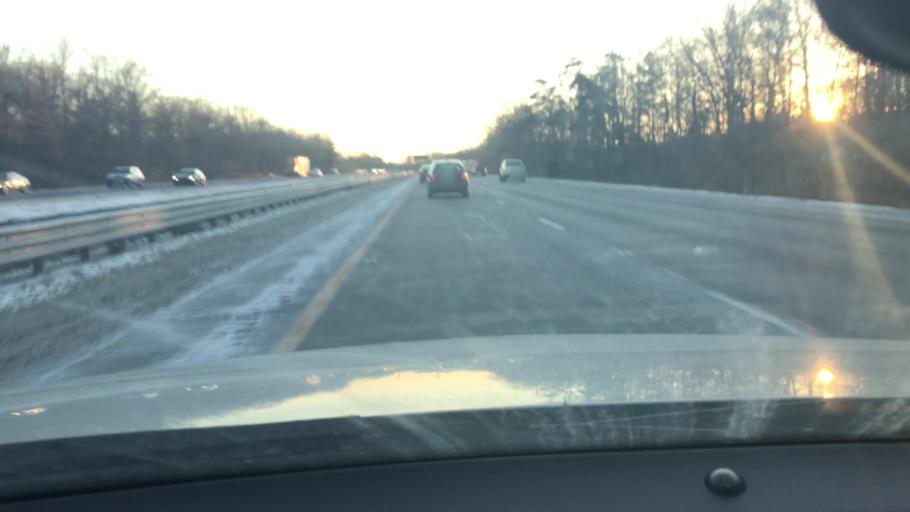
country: US
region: New Jersey
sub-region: Mercer County
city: Mercerville
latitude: 40.2168
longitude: -74.7008
